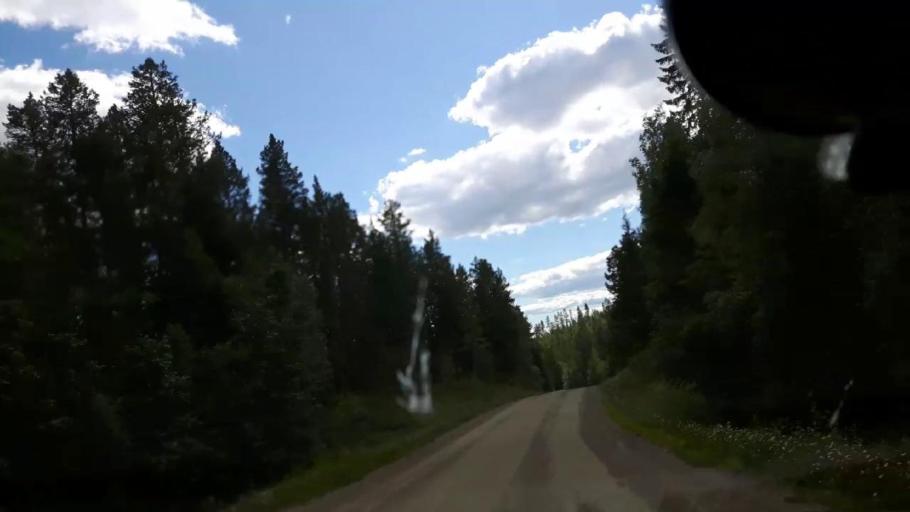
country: SE
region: Vaesternorrland
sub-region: Ange Kommun
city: Ange
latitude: 62.7285
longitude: 15.6426
